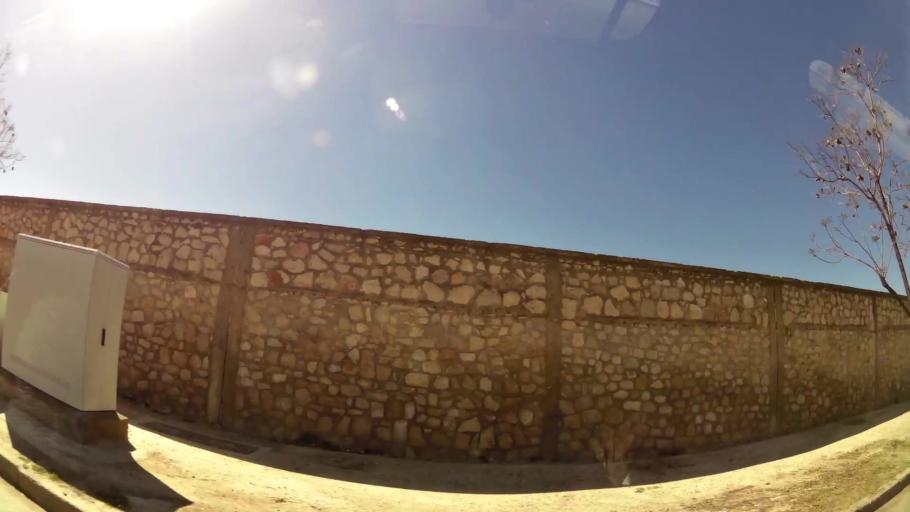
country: MA
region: Meknes-Tafilalet
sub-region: Meknes
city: Meknes
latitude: 33.9079
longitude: -5.5447
